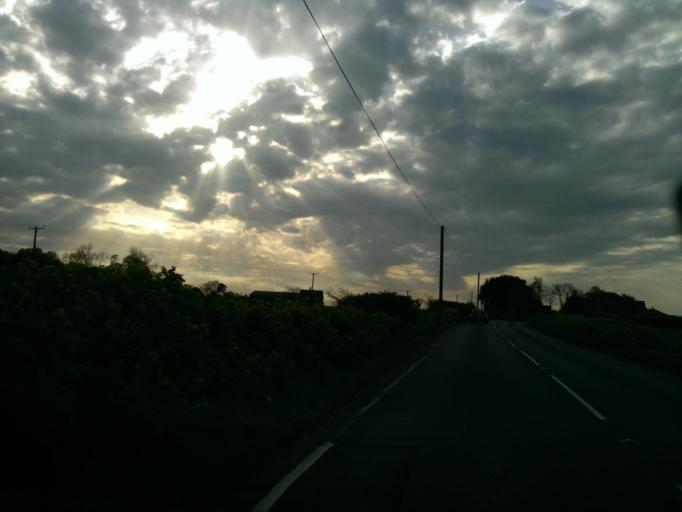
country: GB
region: England
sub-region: Essex
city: Great Bentley
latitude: 51.8365
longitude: 1.0512
